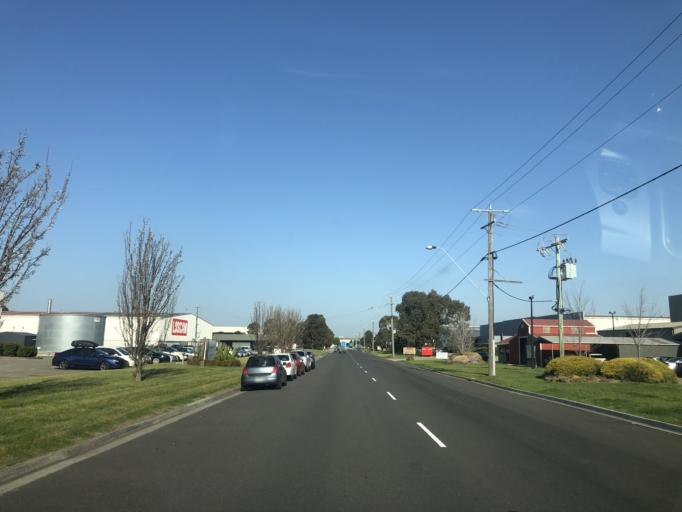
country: AU
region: Victoria
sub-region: Casey
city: Eumemmerring
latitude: -38.0094
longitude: 145.2380
